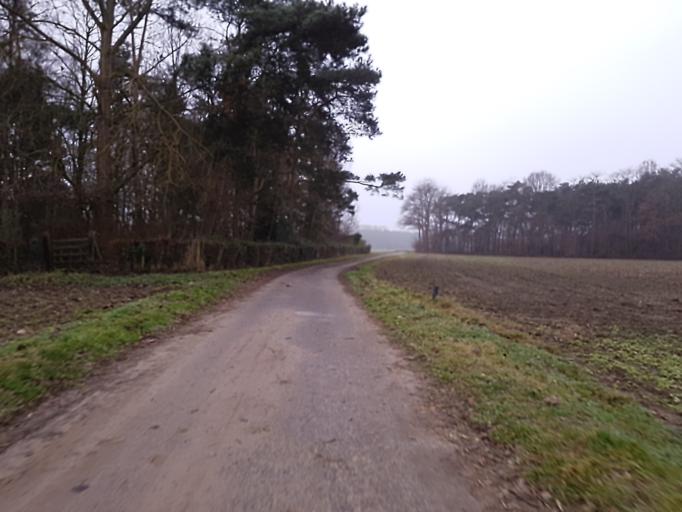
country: BE
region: Flanders
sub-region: Provincie Vlaams-Brabant
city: Keerbergen
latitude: 50.9907
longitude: 4.6085
